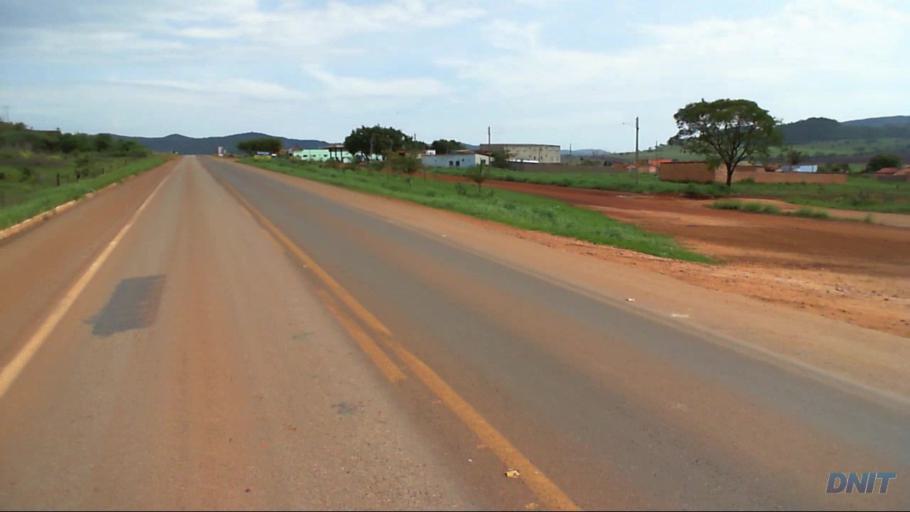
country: BR
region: Goias
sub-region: Barro Alto
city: Barro Alto
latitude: -14.9702
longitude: -48.9306
